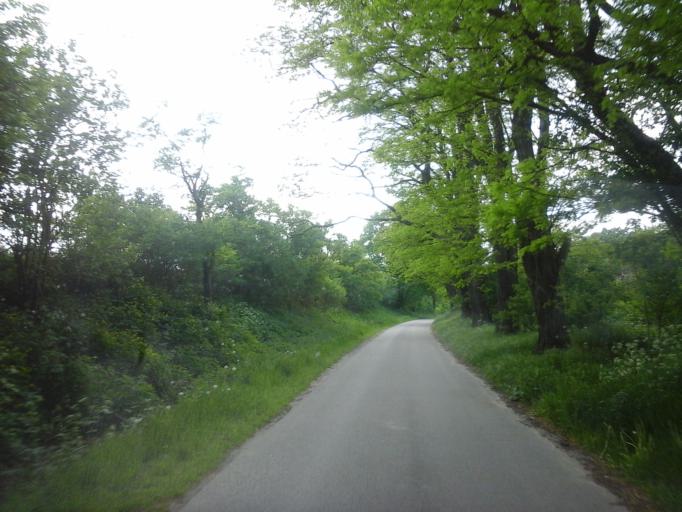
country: PL
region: West Pomeranian Voivodeship
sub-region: Powiat mysliborski
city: Barlinek
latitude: 53.0457
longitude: 15.2393
